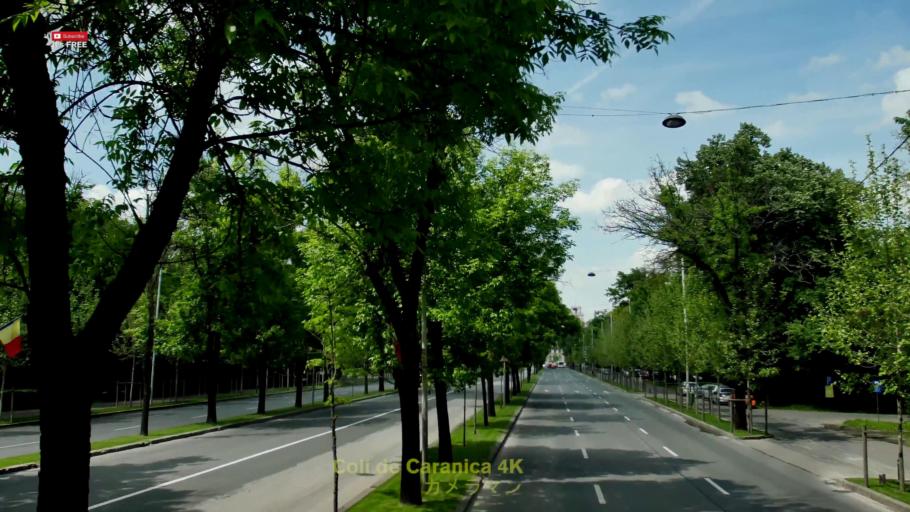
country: RO
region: Bucuresti
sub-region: Municipiul Bucuresti
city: Bucuresti
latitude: 44.4753
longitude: 26.0742
